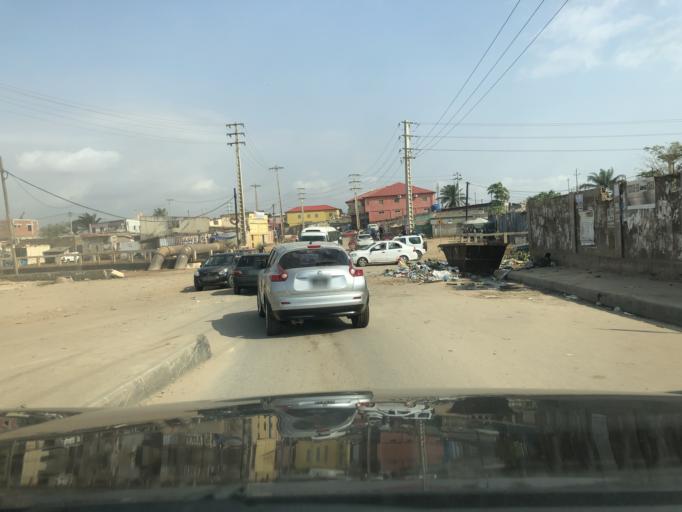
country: AO
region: Luanda
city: Luanda
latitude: -8.8511
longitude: 13.2571
